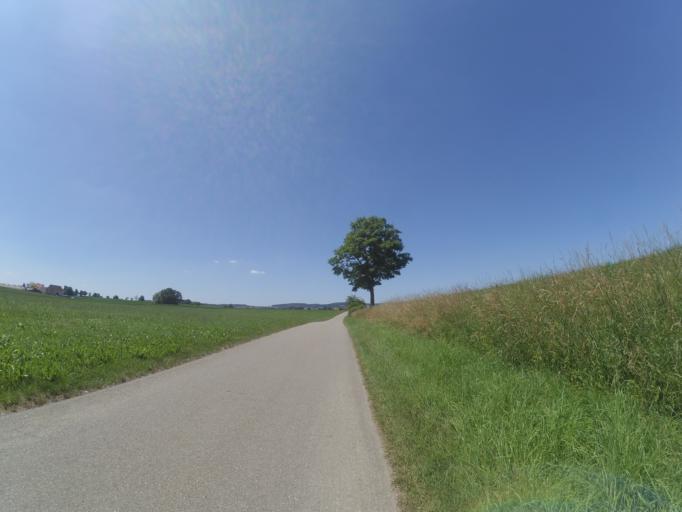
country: DE
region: Baden-Wuerttemberg
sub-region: Tuebingen Region
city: Aulendorf
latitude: 47.9329
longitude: 9.6649
